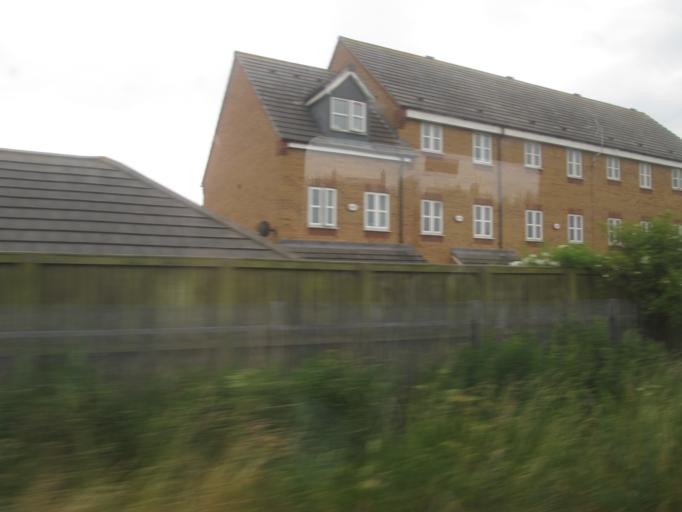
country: GB
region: England
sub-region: Northamptonshire
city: Desborough
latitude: 52.4447
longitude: -0.8095
